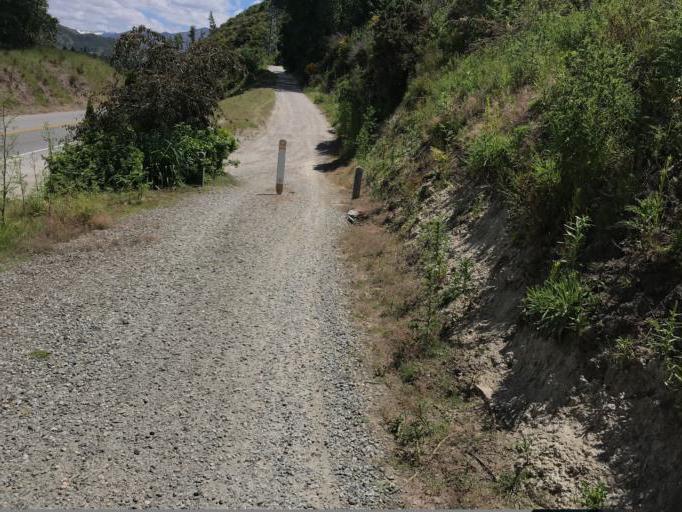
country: NZ
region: Otago
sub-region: Queenstown-Lakes District
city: Arrowtown
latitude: -45.0077
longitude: 168.8848
